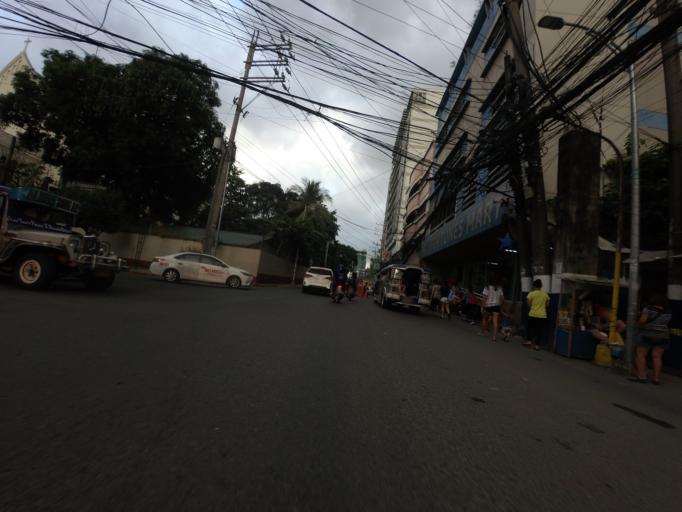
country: PH
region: Metro Manila
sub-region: City of Manila
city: Port Area
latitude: 14.5630
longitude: 120.9960
